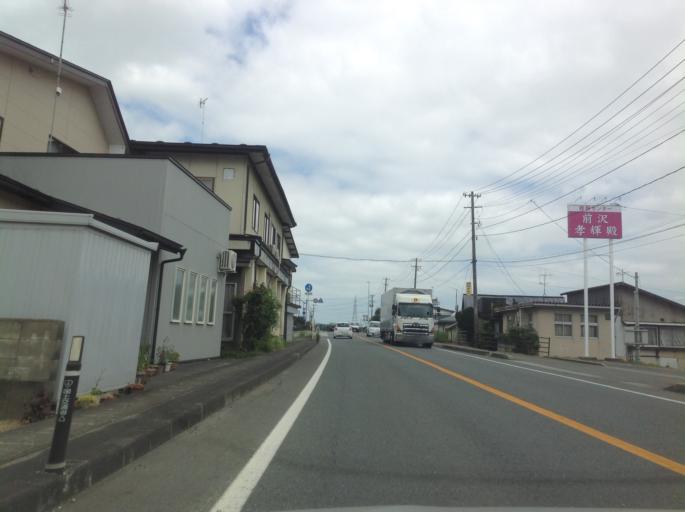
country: JP
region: Iwate
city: Mizusawa
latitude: 39.0823
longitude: 141.1360
